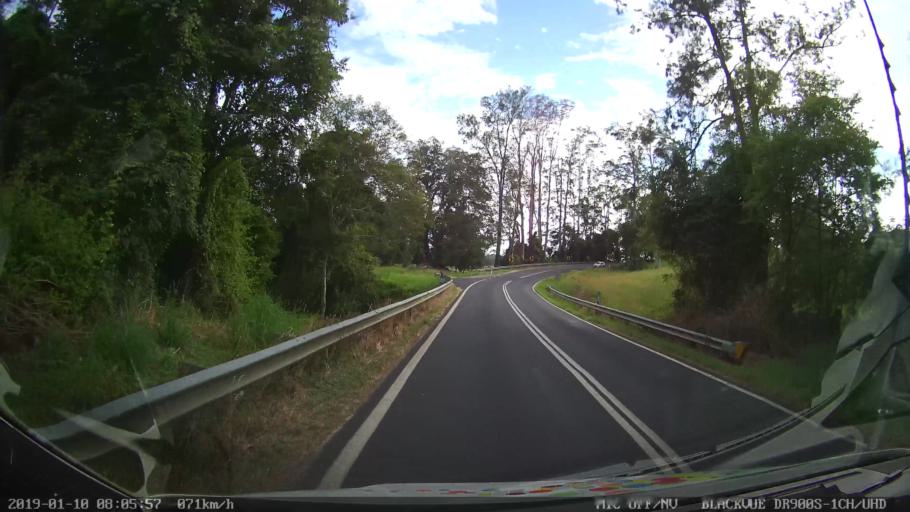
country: AU
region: New South Wales
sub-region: Bellingen
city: Bellingen
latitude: -30.4181
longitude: 152.8475
